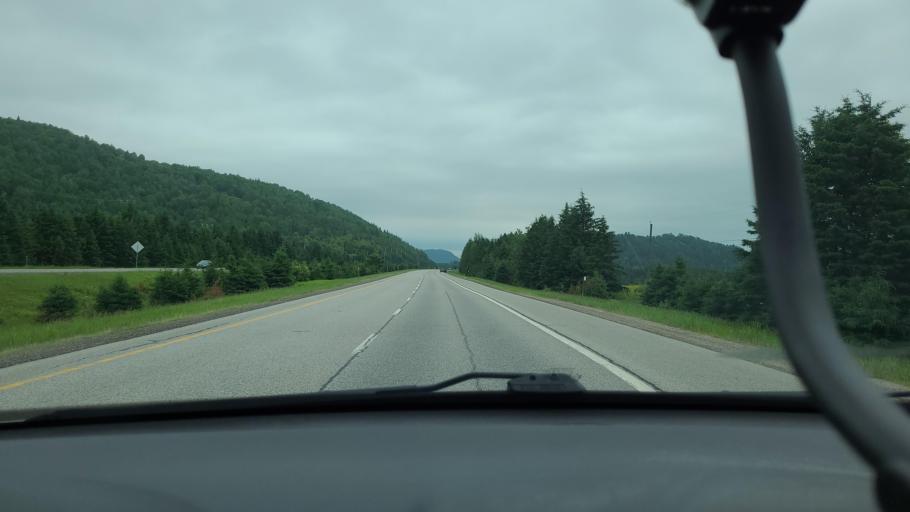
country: CA
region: Quebec
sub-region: Laurentides
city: Labelle
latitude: 46.2049
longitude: -74.7168
